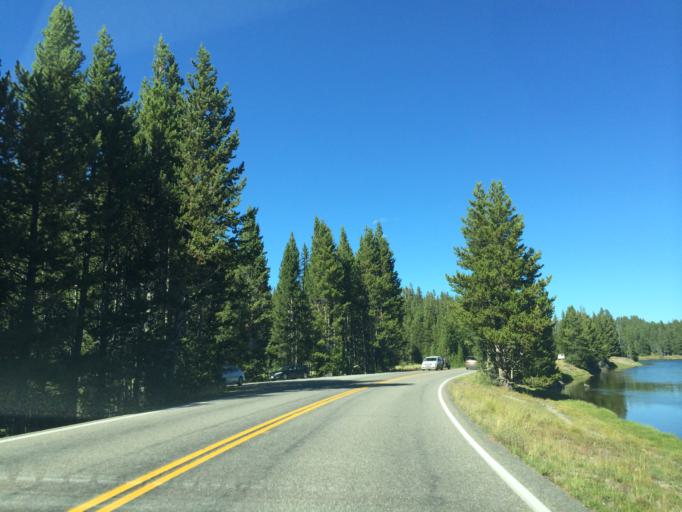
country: US
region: Montana
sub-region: Gallatin County
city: West Yellowstone
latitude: 44.7019
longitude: -110.5061
